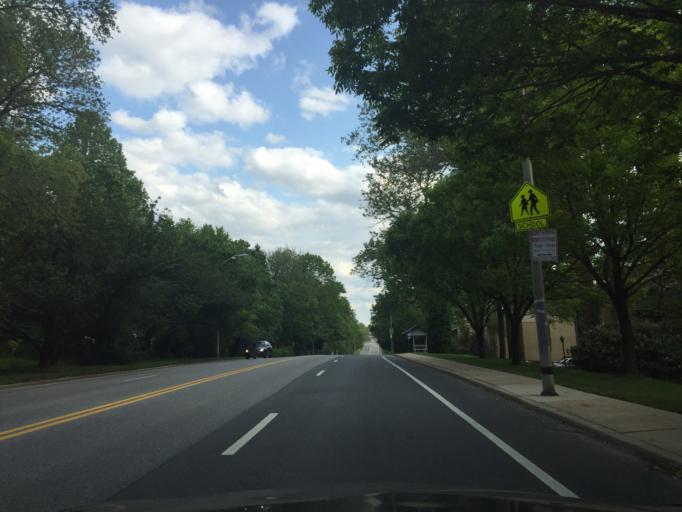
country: US
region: Maryland
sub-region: Baltimore County
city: Towson
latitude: 39.3539
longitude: -76.6437
